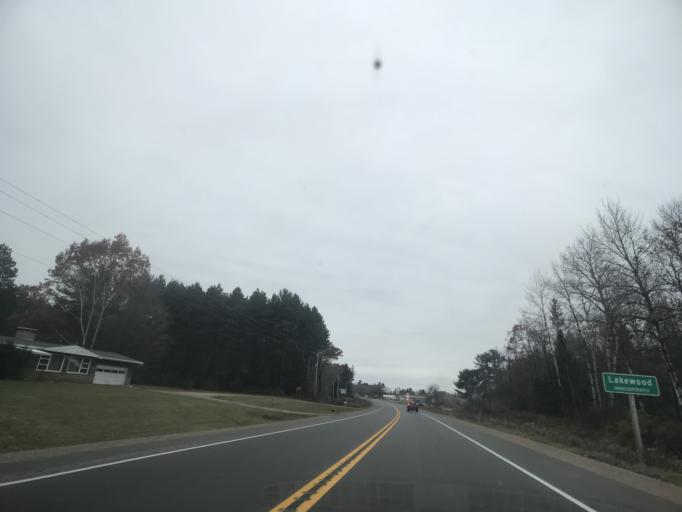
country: US
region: Wisconsin
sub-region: Menominee County
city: Legend Lake
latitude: 45.2962
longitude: -88.5147
